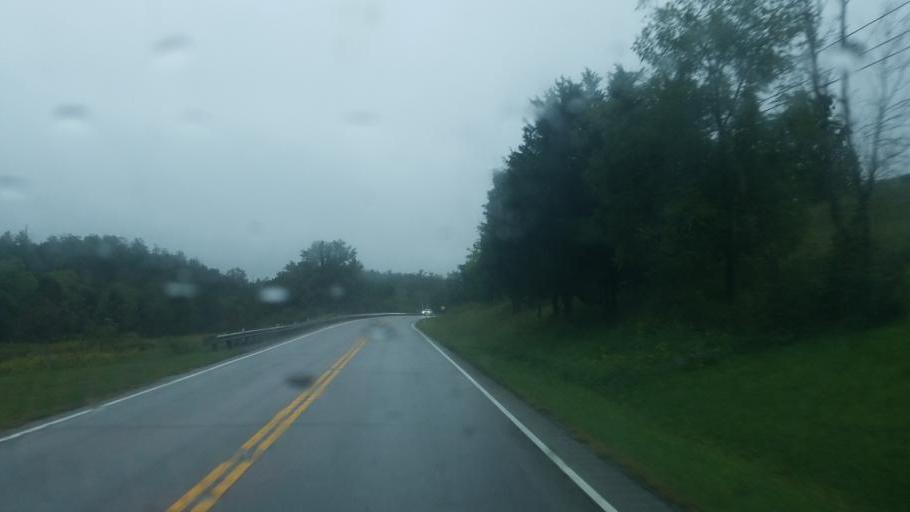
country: US
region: Kentucky
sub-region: Fleming County
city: Flemingsburg
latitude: 38.3778
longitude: -83.6386
